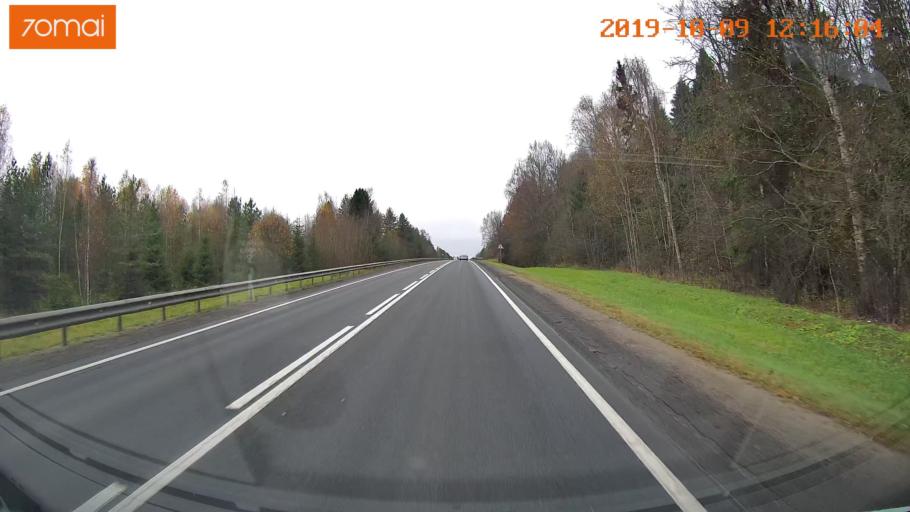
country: RU
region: Jaroslavl
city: Prechistoye
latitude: 58.4739
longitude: 40.3218
